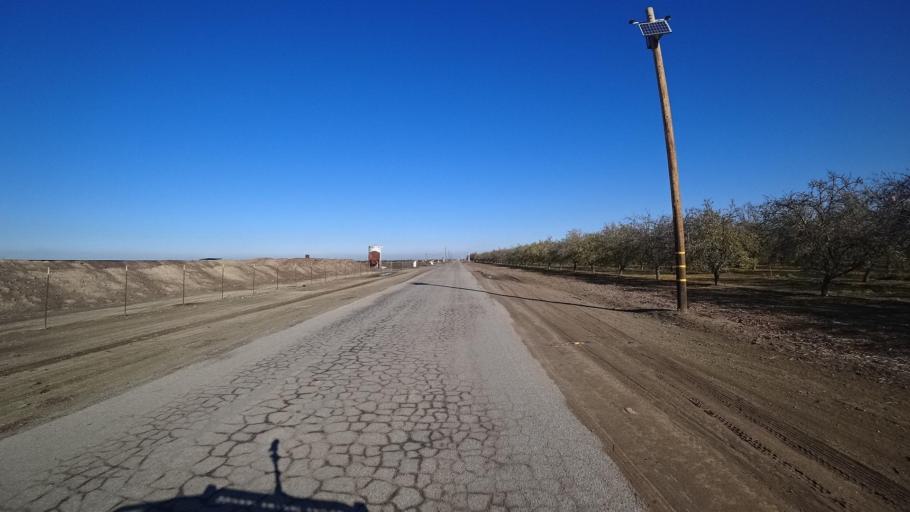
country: US
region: California
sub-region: Kern County
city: McFarland
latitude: 35.6898
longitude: -119.2678
